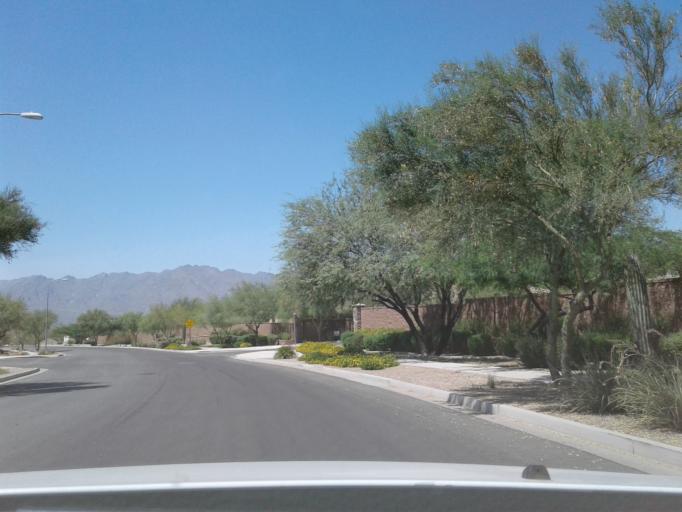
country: US
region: Arizona
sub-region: Maricopa County
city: Laveen
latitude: 33.2955
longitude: -112.1288
